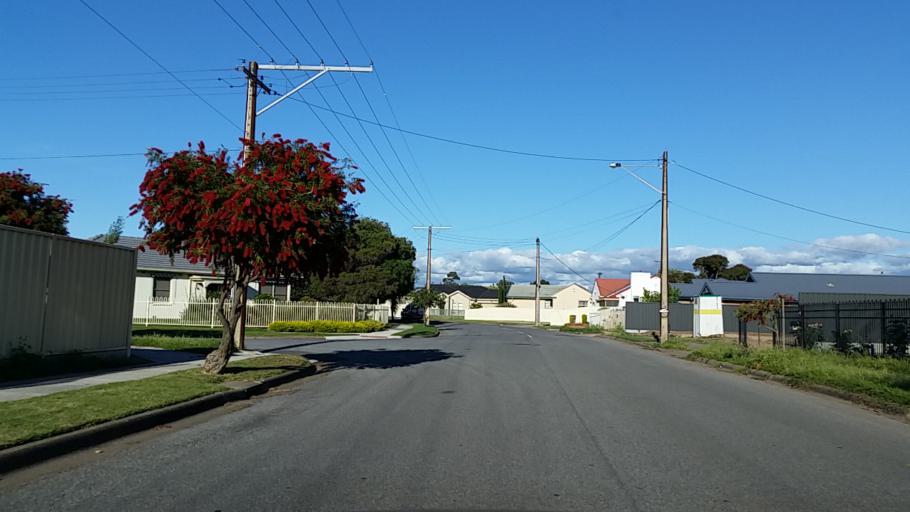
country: AU
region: South Australia
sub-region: Charles Sturt
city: Woodville West
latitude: -34.8869
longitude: 138.5239
